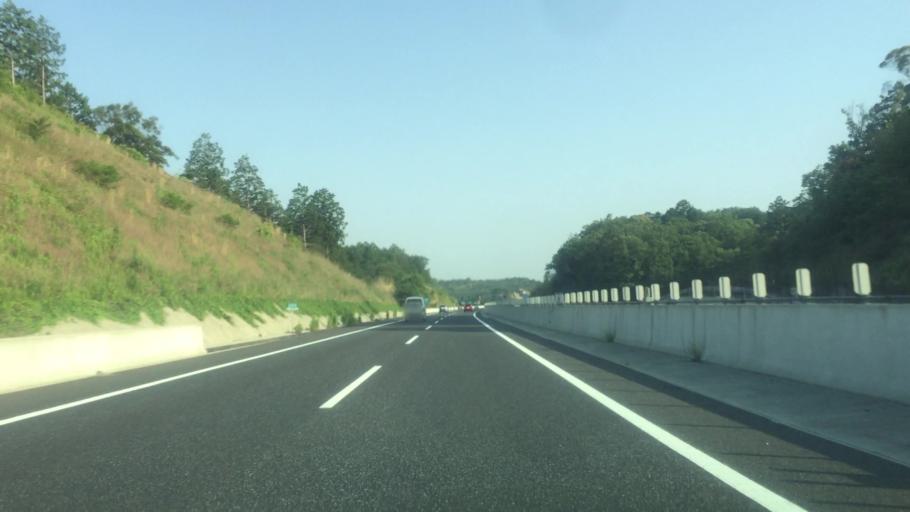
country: JP
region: Aichi
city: Okazaki
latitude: 34.9794
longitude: 137.2418
